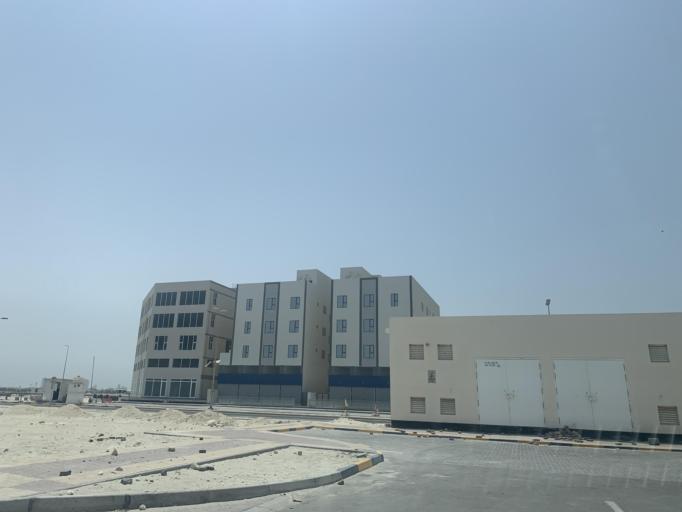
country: BH
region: Muharraq
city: Al Hadd
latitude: 26.2548
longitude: 50.6664
